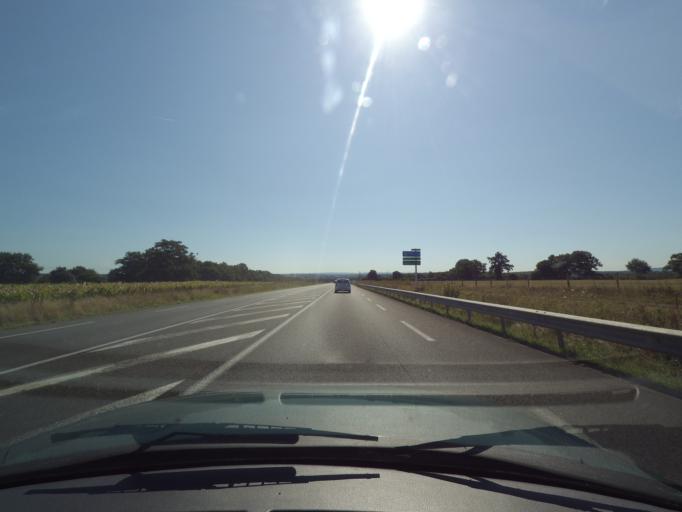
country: FR
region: Limousin
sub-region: Departement de la Haute-Vienne
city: Peyrat-de-Bellac
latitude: 46.1285
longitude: 0.9930
